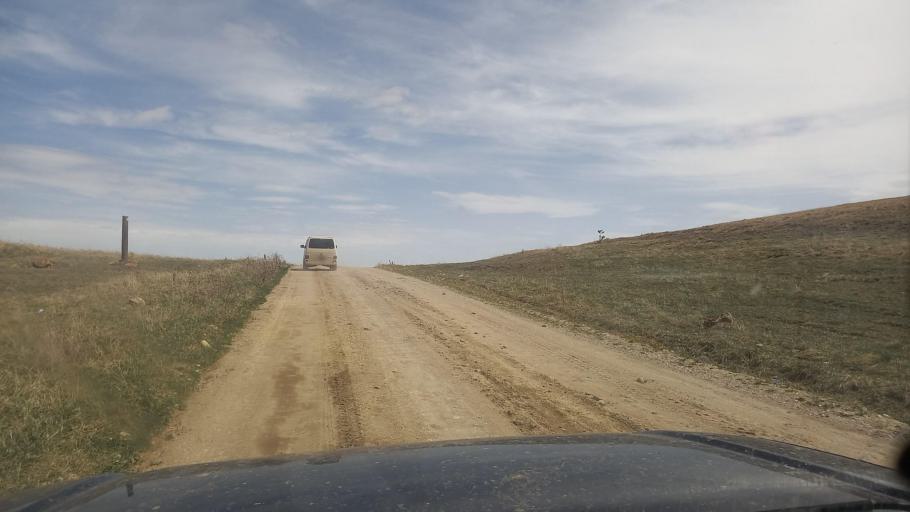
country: RU
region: Stavropol'skiy
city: Kislovodsk
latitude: 43.7504
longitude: 42.7086
